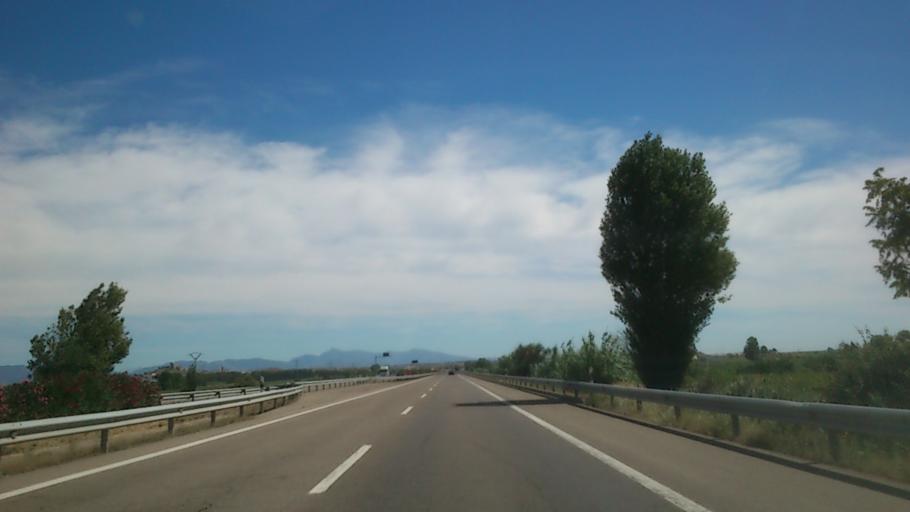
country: ES
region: Aragon
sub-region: Provincia de Huesca
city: Almudebar
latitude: 42.0229
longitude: -0.6051
